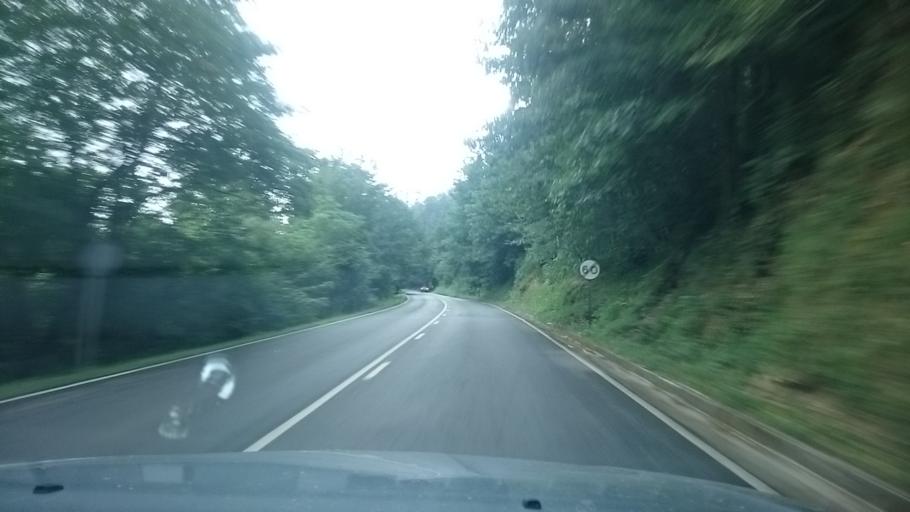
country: ES
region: Asturias
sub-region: Province of Asturias
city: Carrena
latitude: 43.4030
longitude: -4.8923
